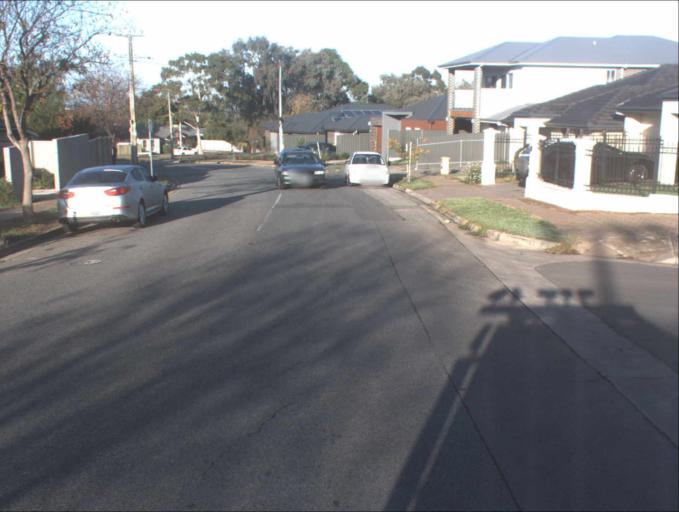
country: AU
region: South Australia
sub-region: Campbelltown
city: Paradise
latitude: -34.8700
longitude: 138.6517
